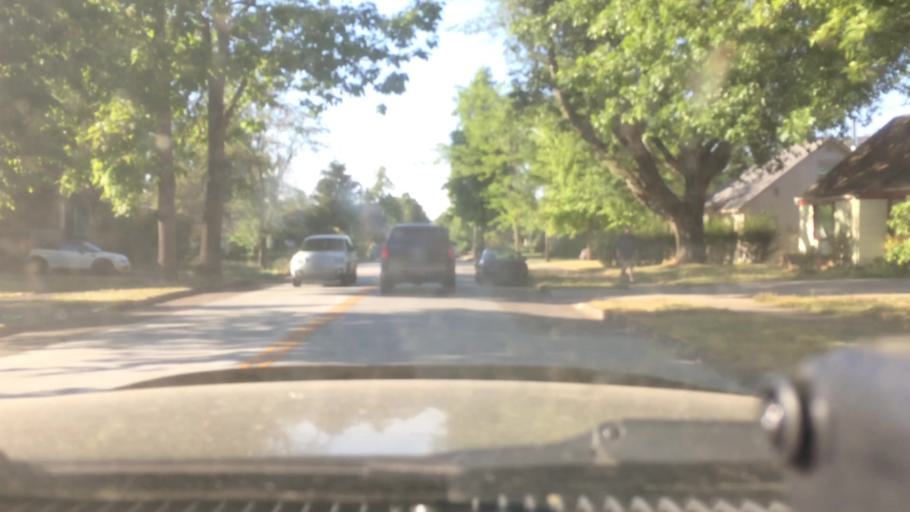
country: US
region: Oregon
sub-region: Lane County
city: Eugene
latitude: 44.0417
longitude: -123.1013
